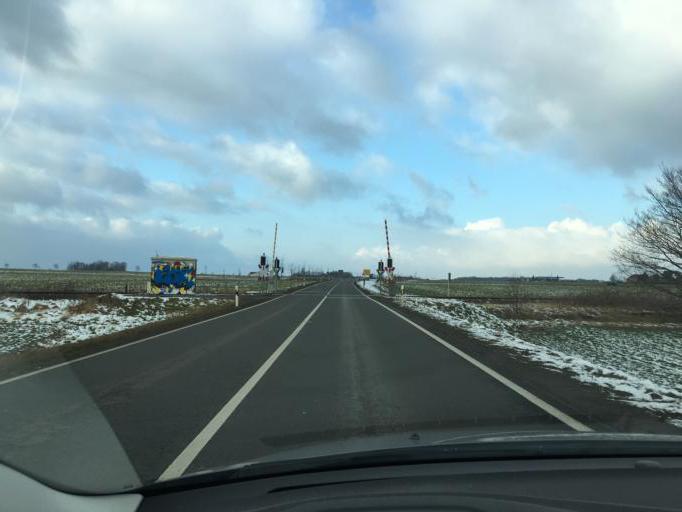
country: DE
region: Saxony
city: Brandis
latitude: 51.3241
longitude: 12.5939
